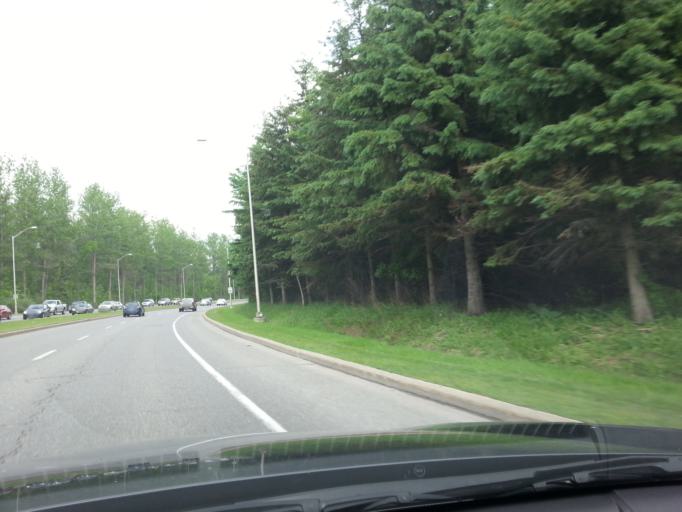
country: CA
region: Ontario
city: Ottawa
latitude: 45.3322
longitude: -75.7370
